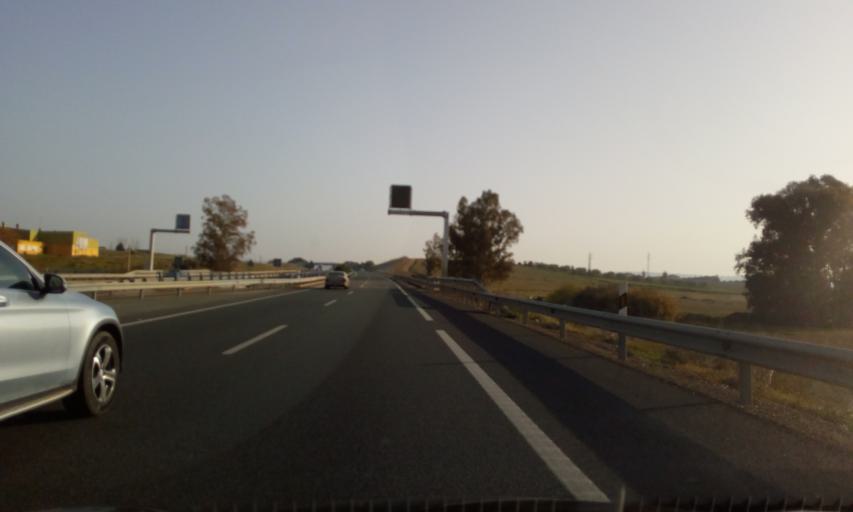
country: ES
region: Andalusia
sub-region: Provincia de Sevilla
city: Aznalcazar
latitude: 37.3624
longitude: -6.2654
